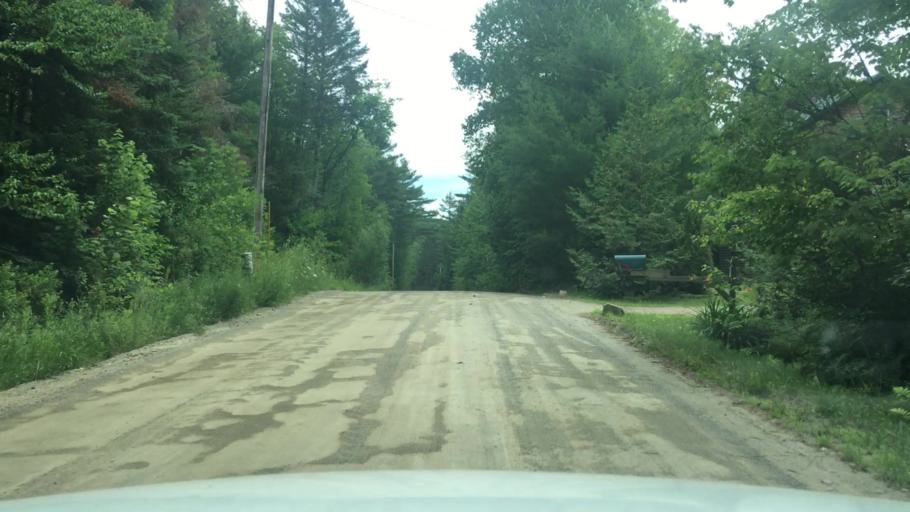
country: US
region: Maine
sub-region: Kennebec County
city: Albion
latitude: 44.4583
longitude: -69.3316
